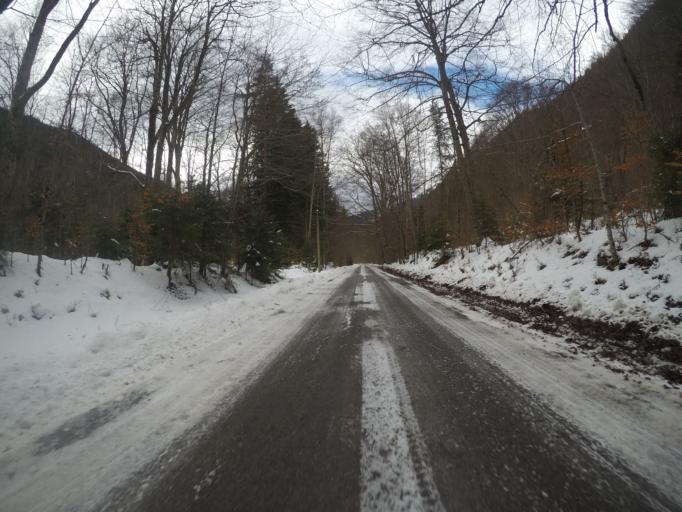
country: BG
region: Kyustendil
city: Sapareva Banya
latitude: 42.1489
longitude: 23.3733
